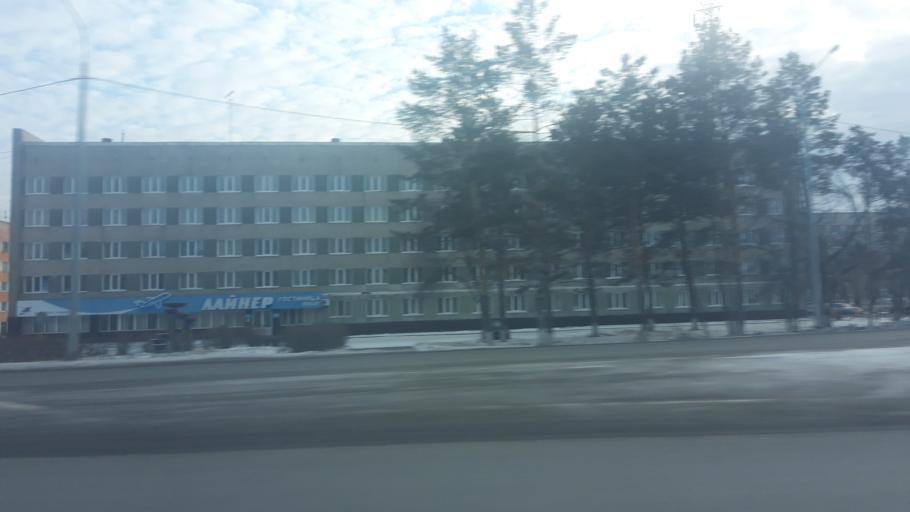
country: RU
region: Tjumen
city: Moskovskiy
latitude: 57.1837
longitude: 65.3527
